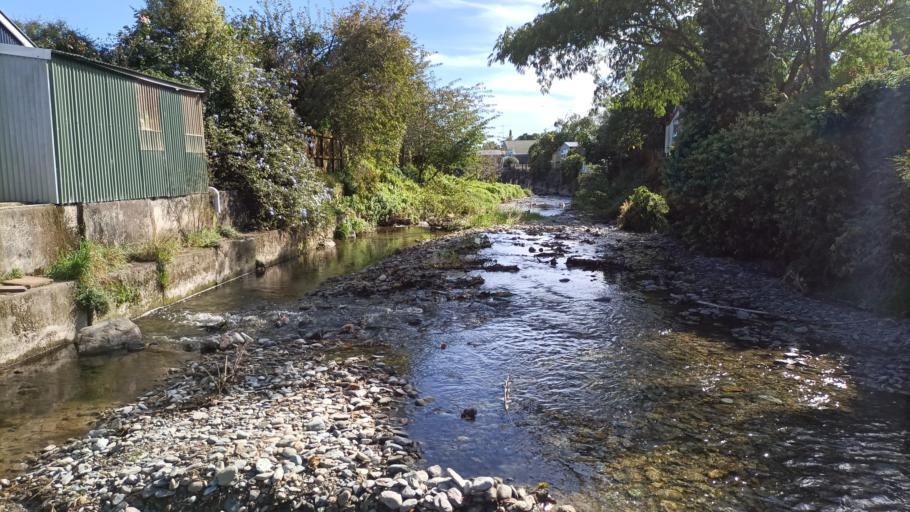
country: NZ
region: Nelson
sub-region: Nelson City
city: Nelson
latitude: -41.2817
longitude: 173.2906
